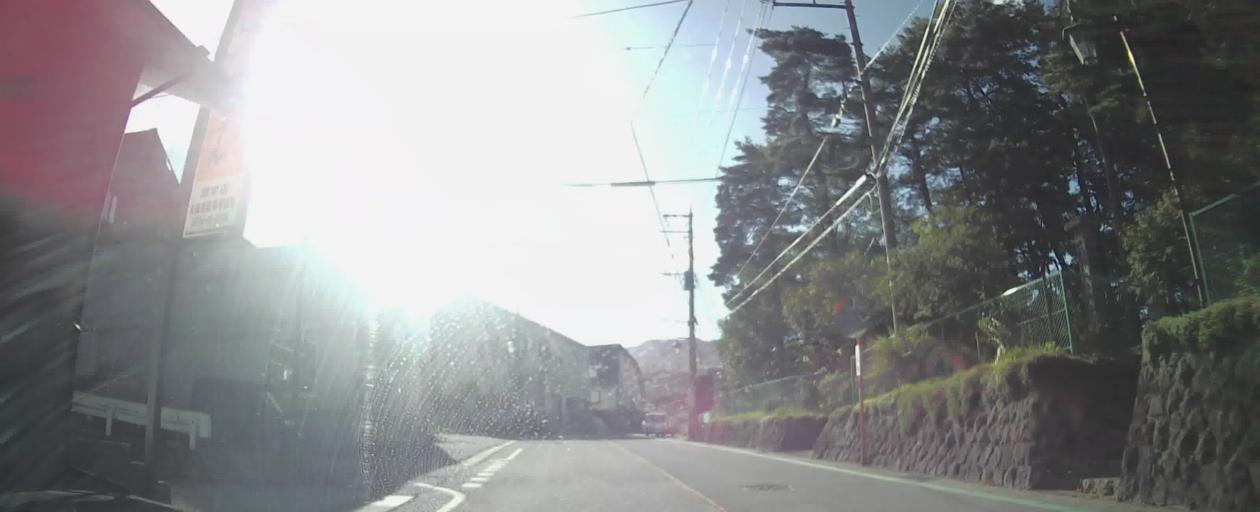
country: JP
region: Gunma
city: Nakanojomachi
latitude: 36.6221
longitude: 138.6051
